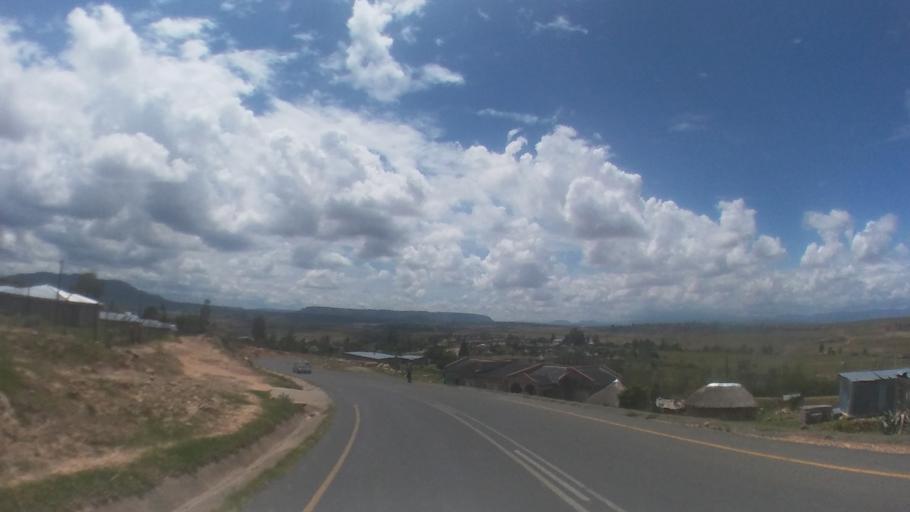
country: LS
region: Maseru
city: Maseru
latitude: -29.4209
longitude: 27.4713
